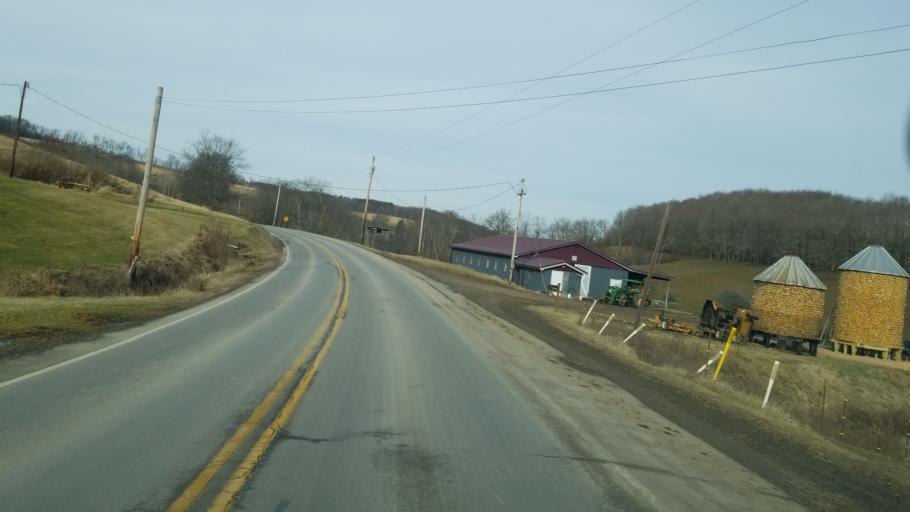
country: US
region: Pennsylvania
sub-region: Jefferson County
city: Punxsutawney
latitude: 40.8890
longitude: -79.0408
